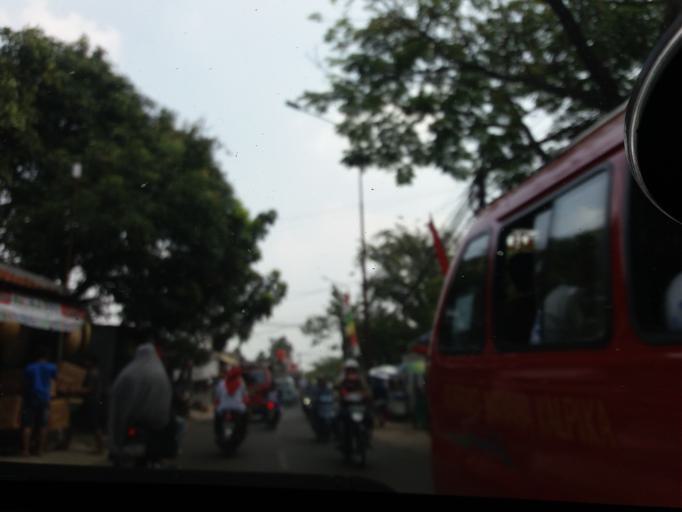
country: ID
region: West Java
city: Depok
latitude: -6.3312
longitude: 106.8308
